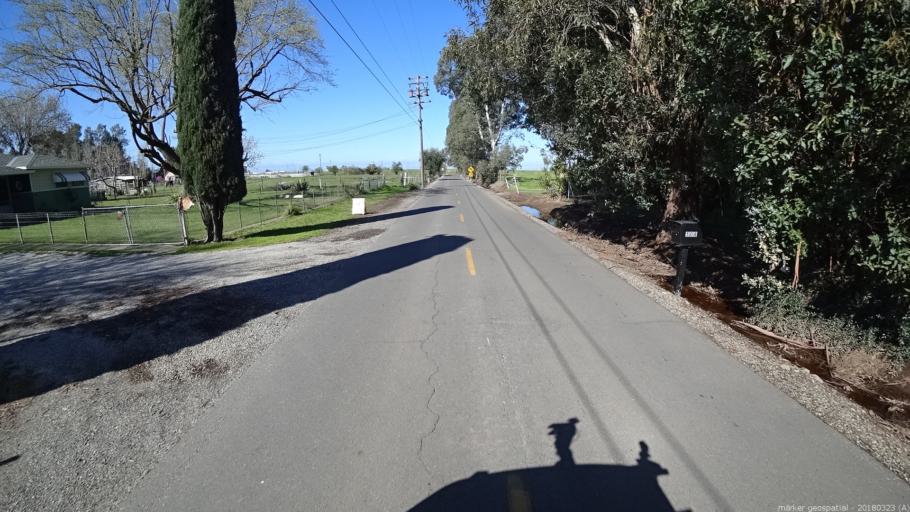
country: US
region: California
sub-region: Sacramento County
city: Elverta
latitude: 38.7052
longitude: -121.4731
